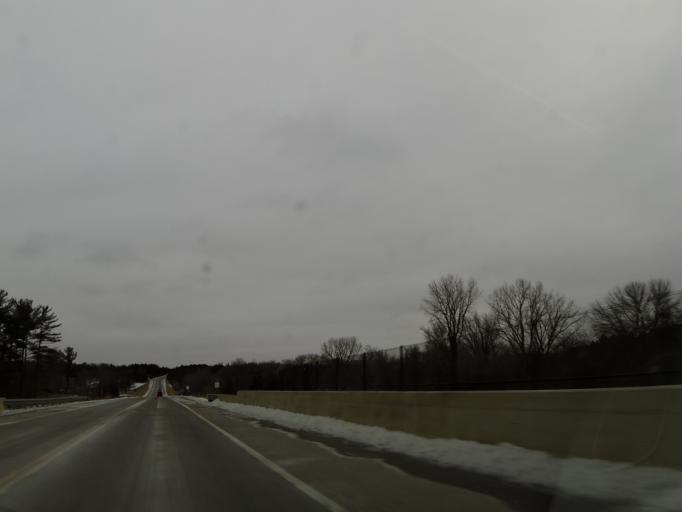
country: US
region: Minnesota
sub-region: Scott County
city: Jordan
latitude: 44.6925
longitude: -93.6421
